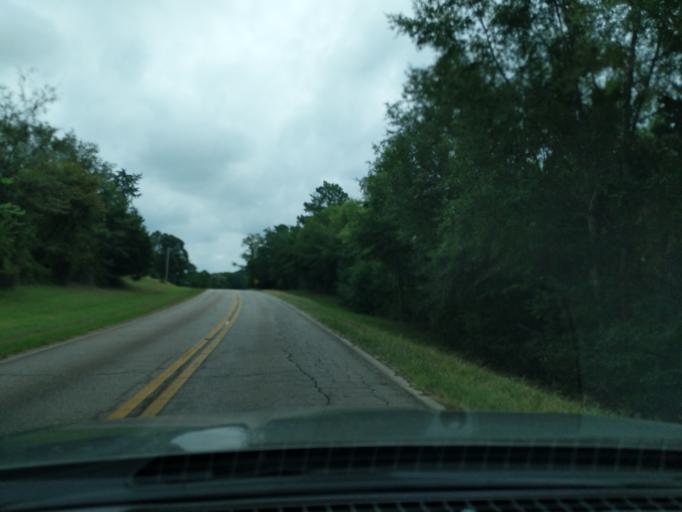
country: US
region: Georgia
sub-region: Columbia County
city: Appling
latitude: 33.5831
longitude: -82.3739
